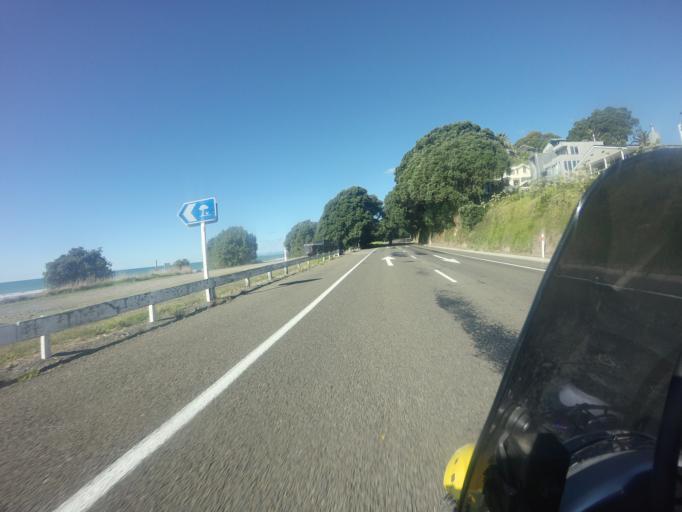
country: NZ
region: Bay of Plenty
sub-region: Opotiki District
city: Opotiki
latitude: -37.9919
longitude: 177.2280
